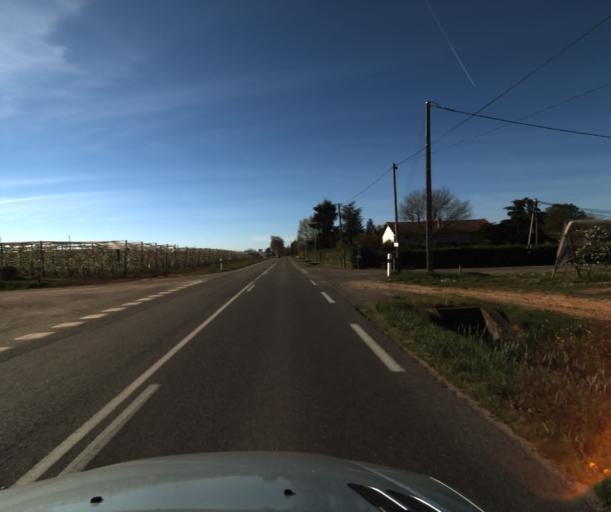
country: FR
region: Midi-Pyrenees
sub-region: Departement du Tarn-et-Garonne
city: Montbeton
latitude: 44.0375
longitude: 1.3095
